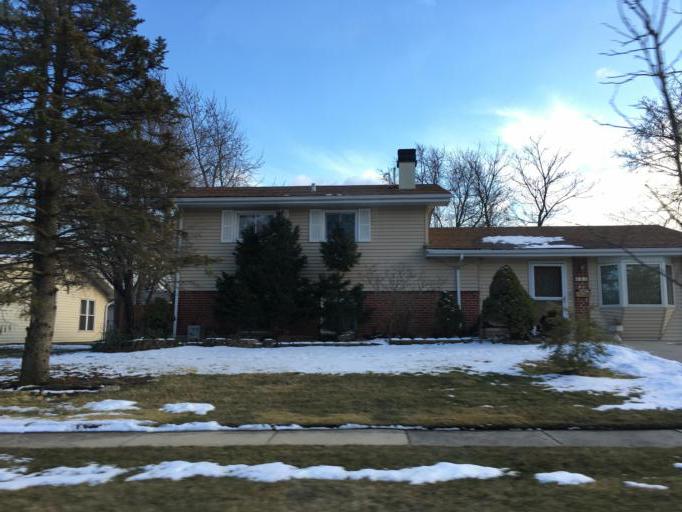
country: US
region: Illinois
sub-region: Cook County
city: Schaumburg
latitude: 42.0423
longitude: -88.0961
